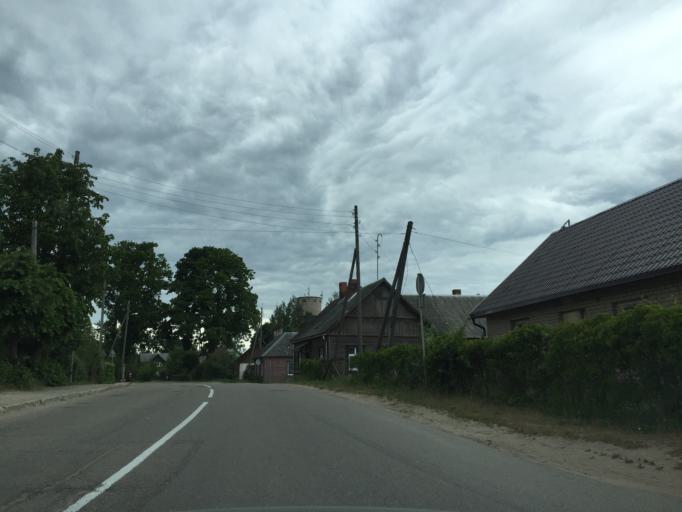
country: LV
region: Rezekne
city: Rezekne
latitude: 56.3470
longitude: 27.1600
